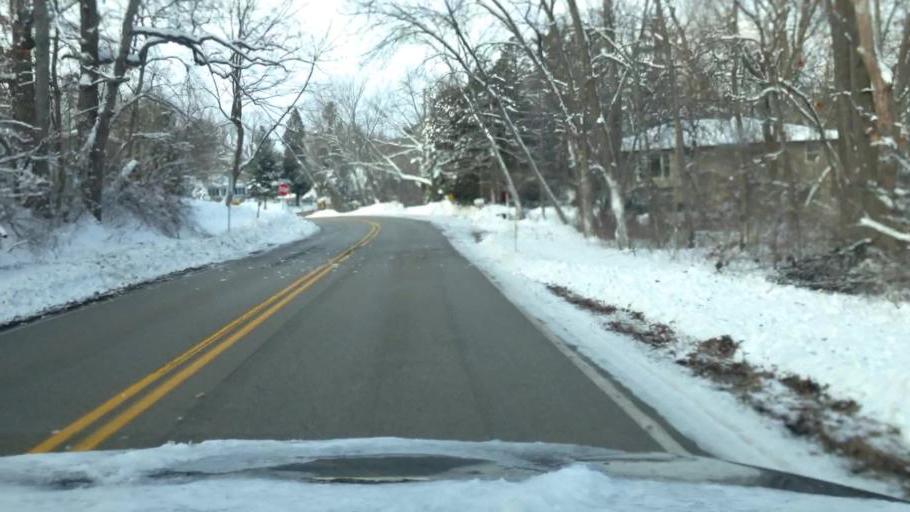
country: US
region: Wisconsin
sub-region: Waukesha County
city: Eagle
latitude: 42.8522
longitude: -88.4339
